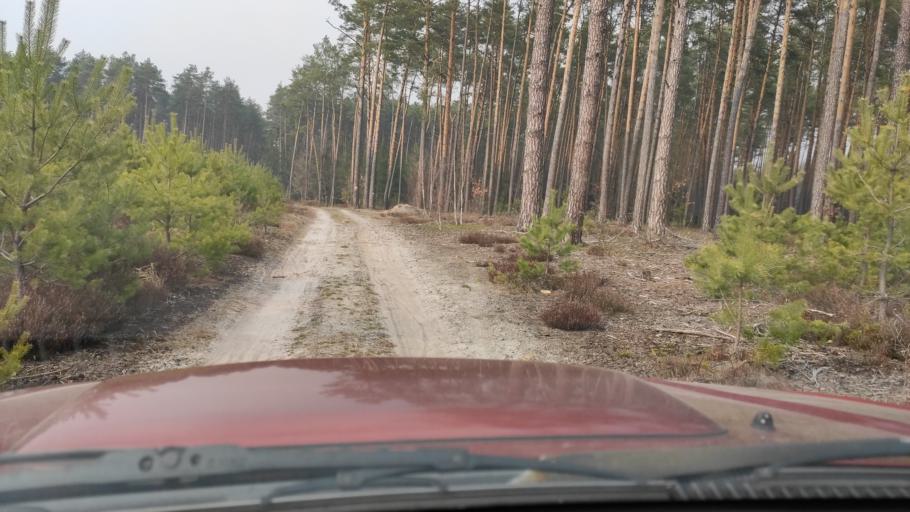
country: PL
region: Masovian Voivodeship
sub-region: Powiat zwolenski
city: Zwolen
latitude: 51.3947
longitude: 21.5720
